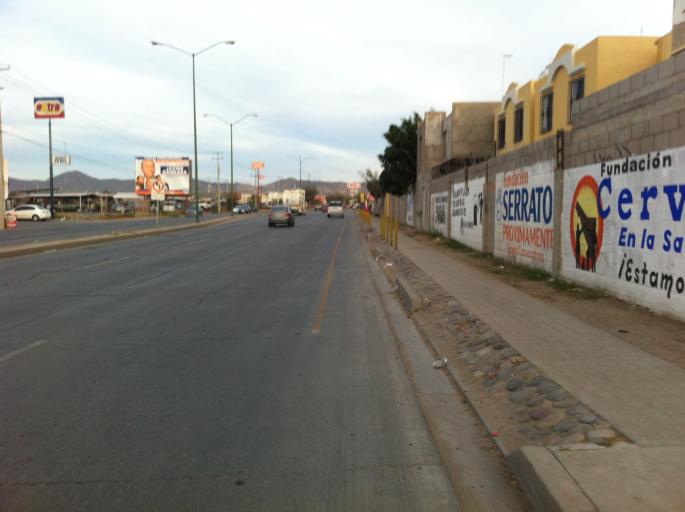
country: MX
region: Sonora
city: Hermosillo
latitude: 29.1163
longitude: -111.0031
